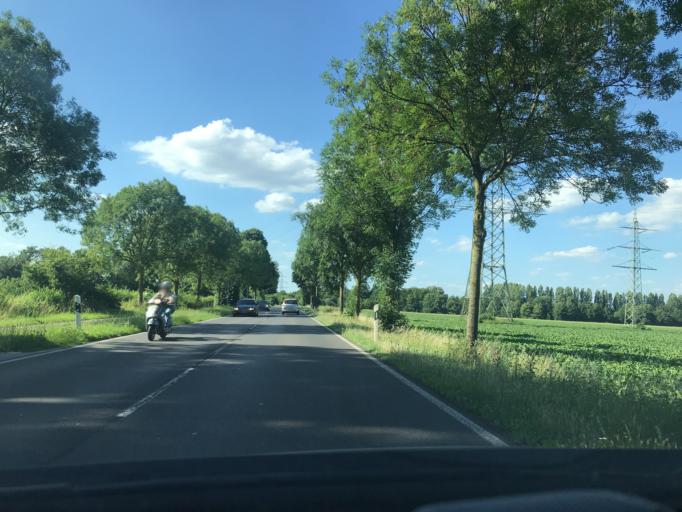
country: DE
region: North Rhine-Westphalia
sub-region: Regierungsbezirk Dusseldorf
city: Neuss
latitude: 51.1568
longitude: 6.6825
